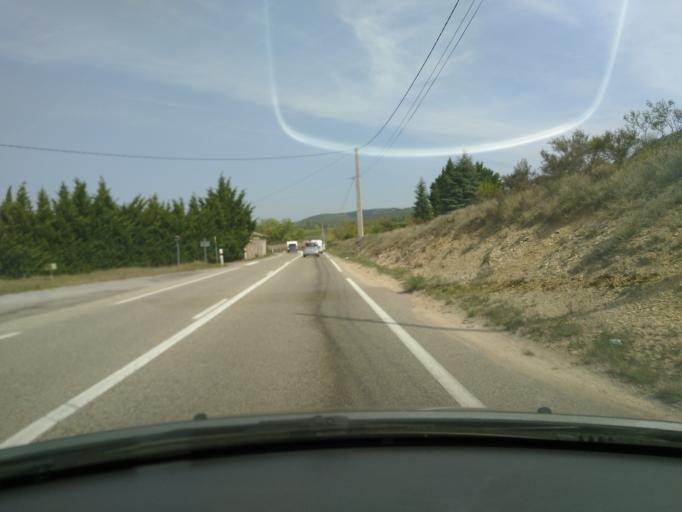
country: FR
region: Rhone-Alpes
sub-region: Departement de l'Ardeche
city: Saint-Sernin
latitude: 44.5284
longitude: 4.4169
